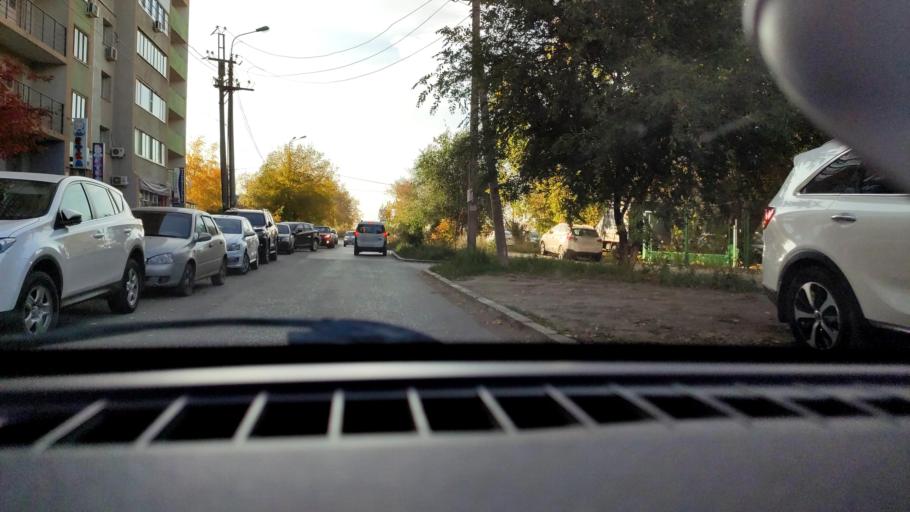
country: RU
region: Samara
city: Samara
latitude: 53.2103
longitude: 50.2043
